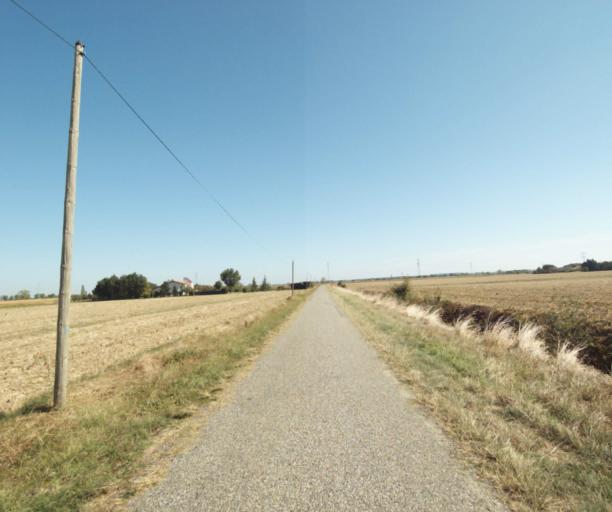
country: FR
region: Midi-Pyrenees
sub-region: Departement du Tarn-et-Garonne
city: Verdun-sur-Garonne
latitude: 43.8326
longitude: 1.2110
